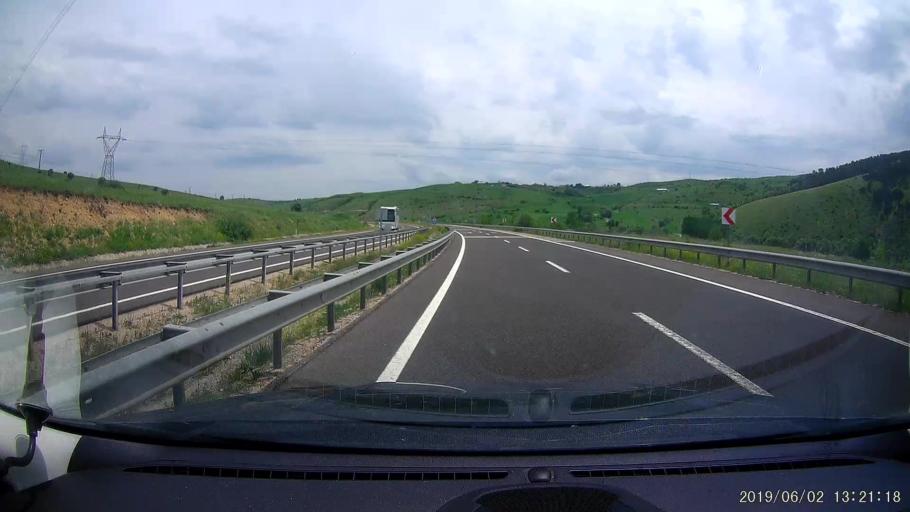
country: TR
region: Cankiri
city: Cerkes
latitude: 40.8350
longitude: 32.7729
